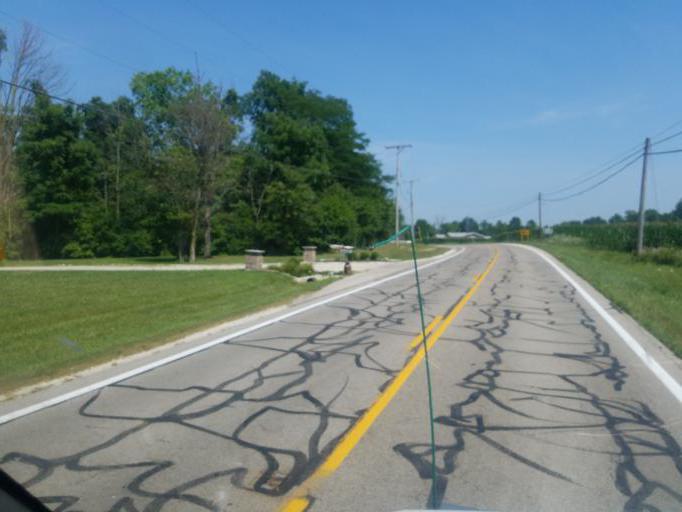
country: US
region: Ohio
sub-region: Mercer County
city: Celina
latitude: 40.4920
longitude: -84.5549
